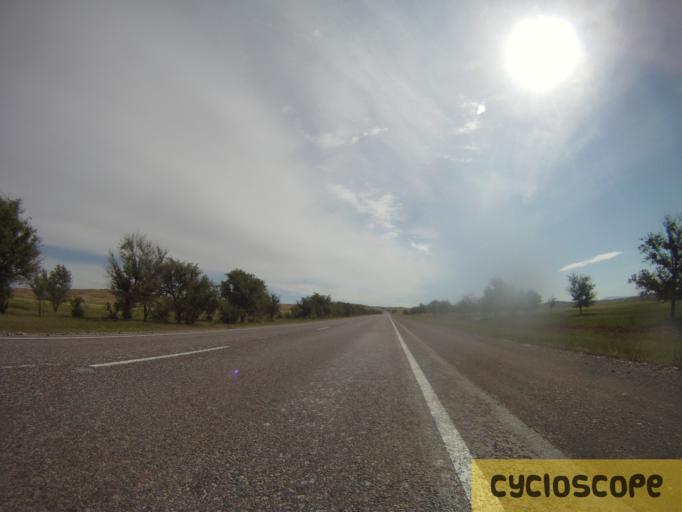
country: KZ
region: Zhambyl
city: Georgiyevka
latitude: 43.2508
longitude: 74.8023
